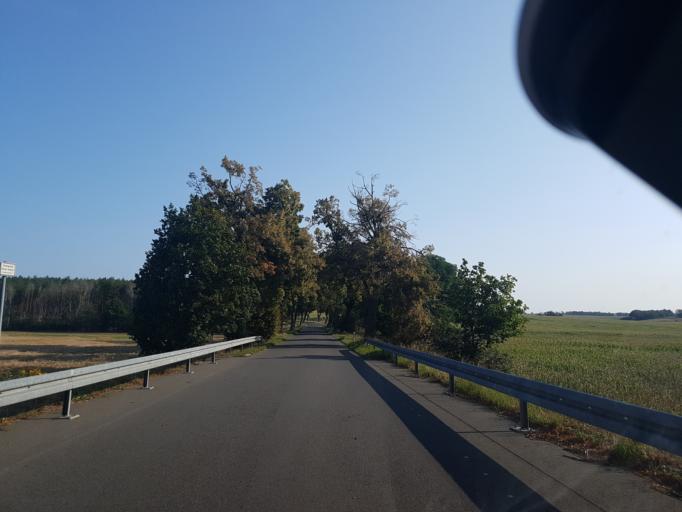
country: DE
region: Brandenburg
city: Niemegk
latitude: 52.0019
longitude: 12.6815
